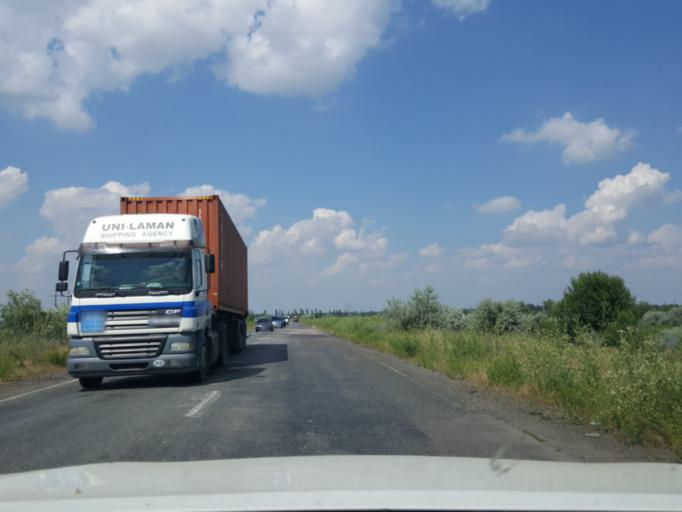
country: UA
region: Odessa
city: Bilyayivka
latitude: 46.4058
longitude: 30.1048
